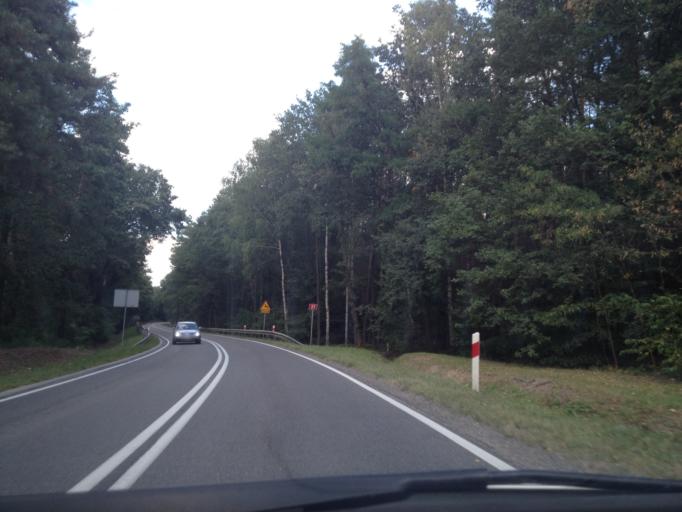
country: PL
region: Lubusz
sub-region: Powiat zarski
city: Sieniawa Zarska
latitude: 51.5839
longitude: 15.0766
